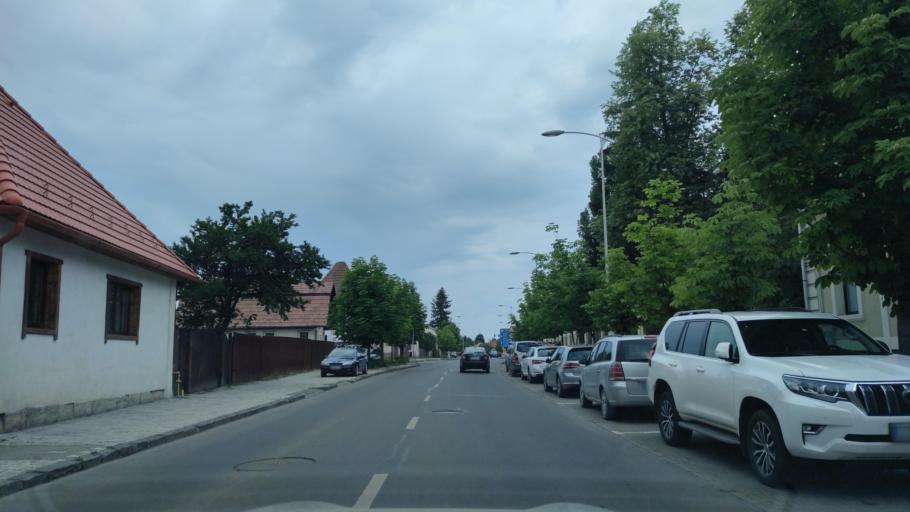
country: RO
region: Harghita
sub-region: Municipiul Miercurea Ciuc
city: Miercurea-Ciuc
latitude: 46.3664
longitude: 25.8061
